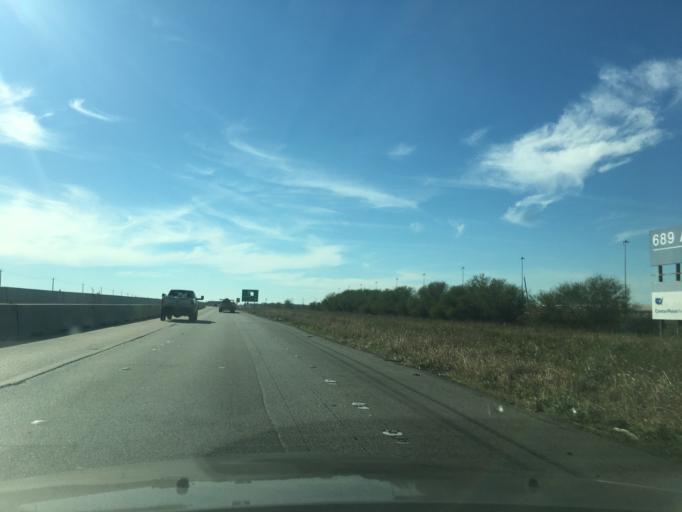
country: US
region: Texas
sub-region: Wharton County
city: East Bernard
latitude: 29.4635
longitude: -95.9737
